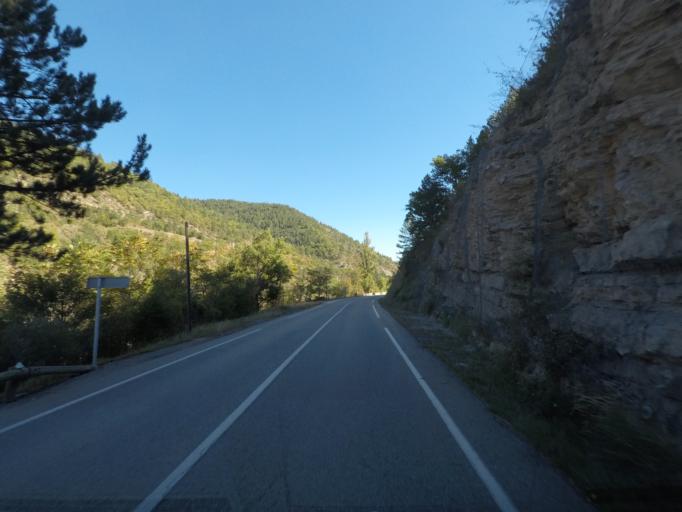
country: FR
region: Rhone-Alpes
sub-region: Departement de la Drome
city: Buis-les-Baronnies
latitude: 44.3867
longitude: 5.3912
